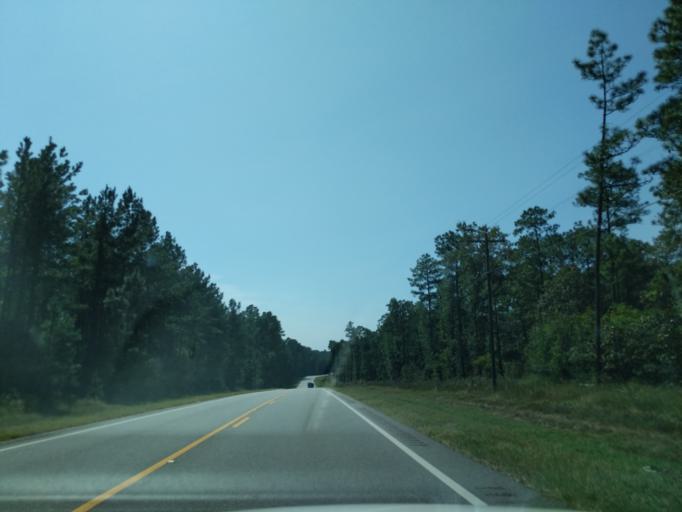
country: US
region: Alabama
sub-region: Covington County
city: Andalusia
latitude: 31.2144
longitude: -86.5386
